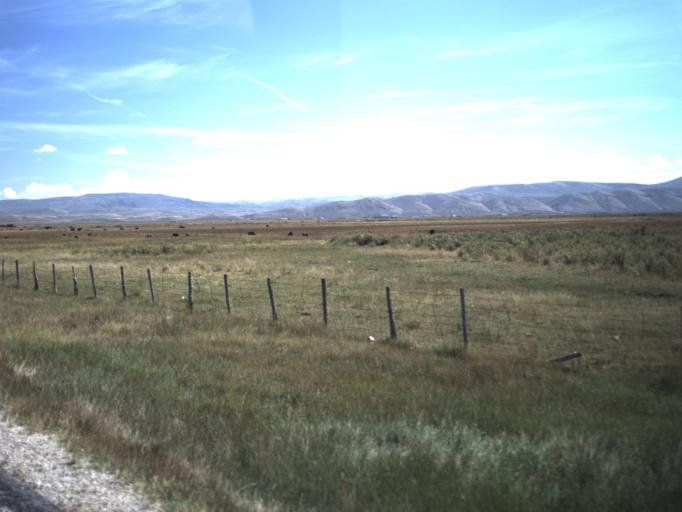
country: US
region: Utah
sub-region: Rich County
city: Randolph
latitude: 41.7735
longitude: -111.1117
